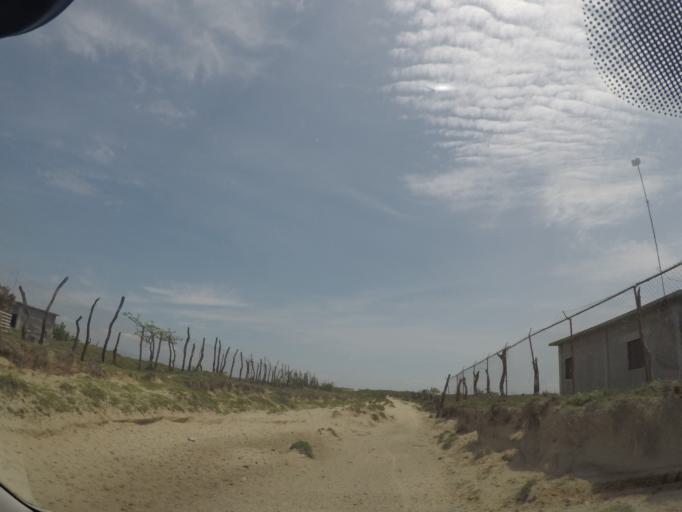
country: MX
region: Oaxaca
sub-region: San Mateo del Mar
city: Colonia Juarez
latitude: 16.2137
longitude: -95.0358
